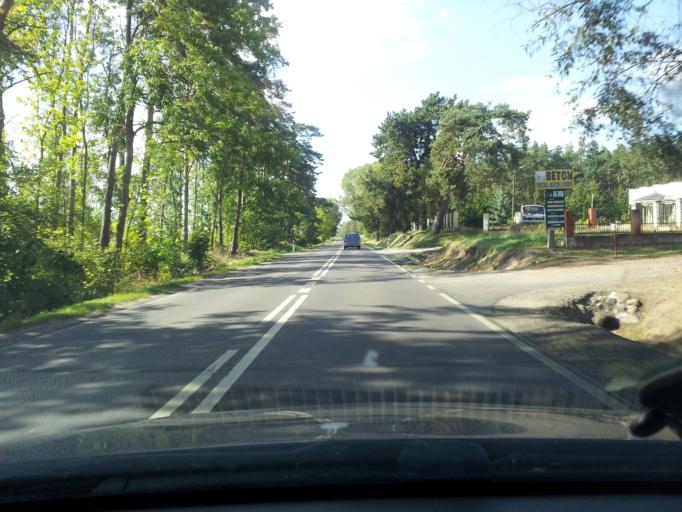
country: PL
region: Kujawsko-Pomorskie
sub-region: Powiat golubsko-dobrzynski
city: Golub-Dobrzyn
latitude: 53.1056
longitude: 19.1240
